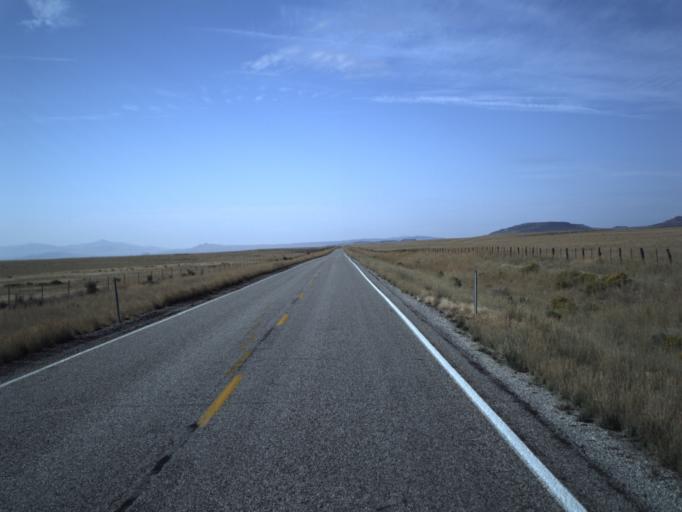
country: US
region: Idaho
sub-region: Oneida County
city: Malad City
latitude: 41.9257
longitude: -113.0924
